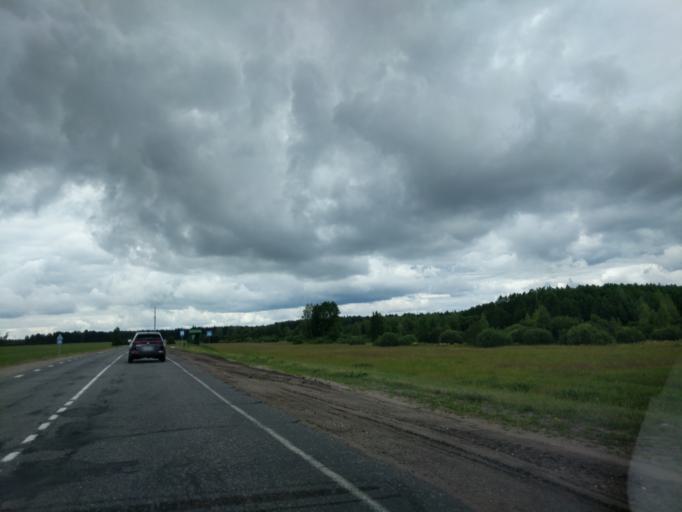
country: BY
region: Minsk
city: Il'ya
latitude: 54.4774
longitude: 27.2570
